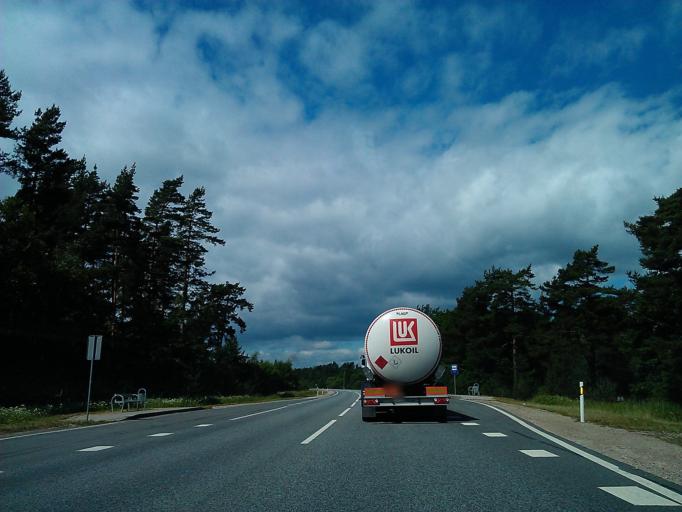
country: LV
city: Tireli
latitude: 56.9289
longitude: 23.6488
